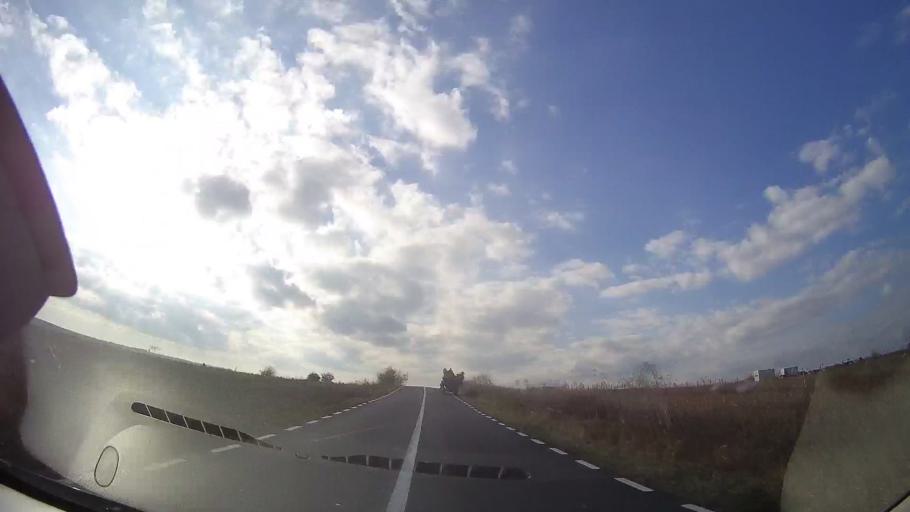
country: RO
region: Constanta
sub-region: Comuna Limanu
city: Limanu
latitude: 43.8231
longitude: 28.4819
